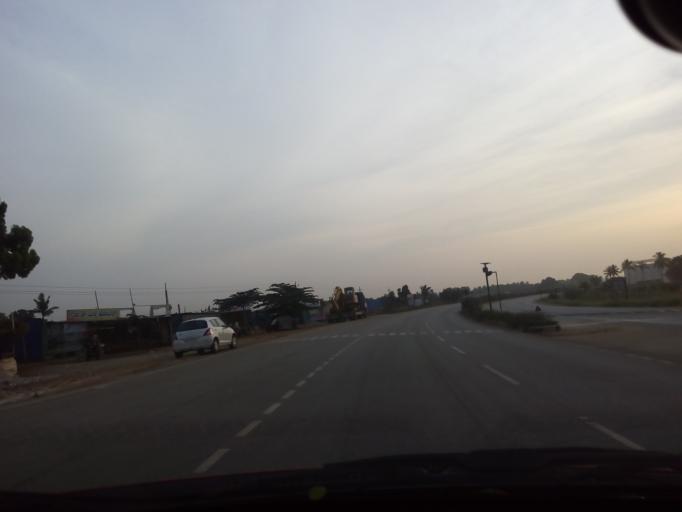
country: IN
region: Karnataka
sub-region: Chikkaballapur
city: Chik Ballapur
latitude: 13.3830
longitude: 77.7269
